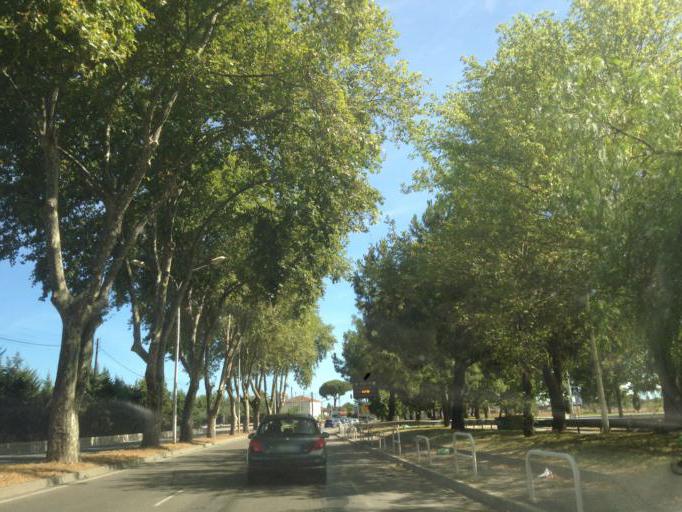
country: FR
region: Provence-Alpes-Cote d'Azur
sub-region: Departement des Alpes-Maritimes
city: Saint-Laurent-du-Var
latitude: 43.6924
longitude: 7.1947
